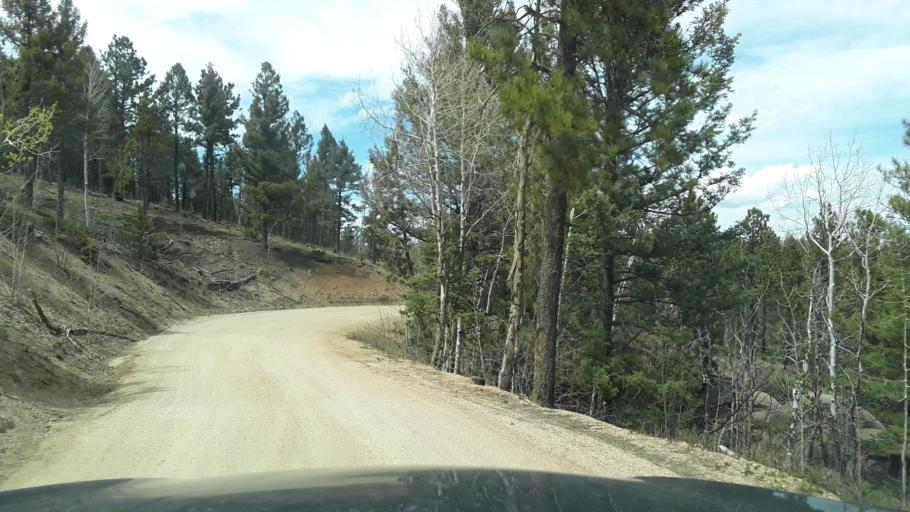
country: US
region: Colorado
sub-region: El Paso County
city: Palmer Lake
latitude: 39.0578
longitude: -104.9759
